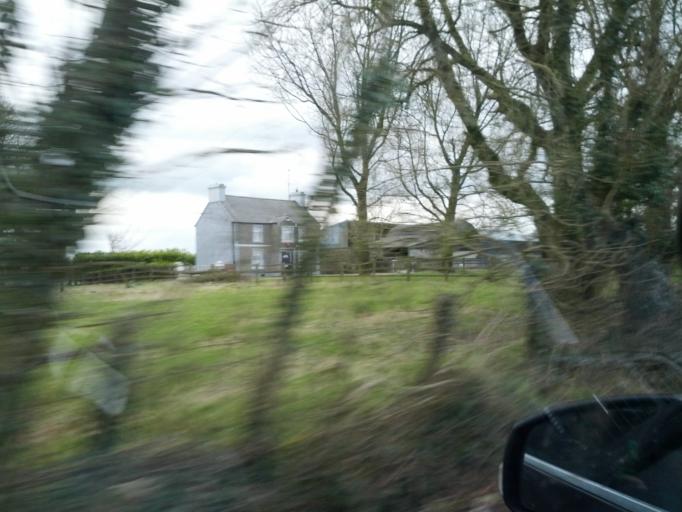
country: IE
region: Connaught
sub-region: County Galway
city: Athenry
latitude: 53.4947
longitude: -8.5982
